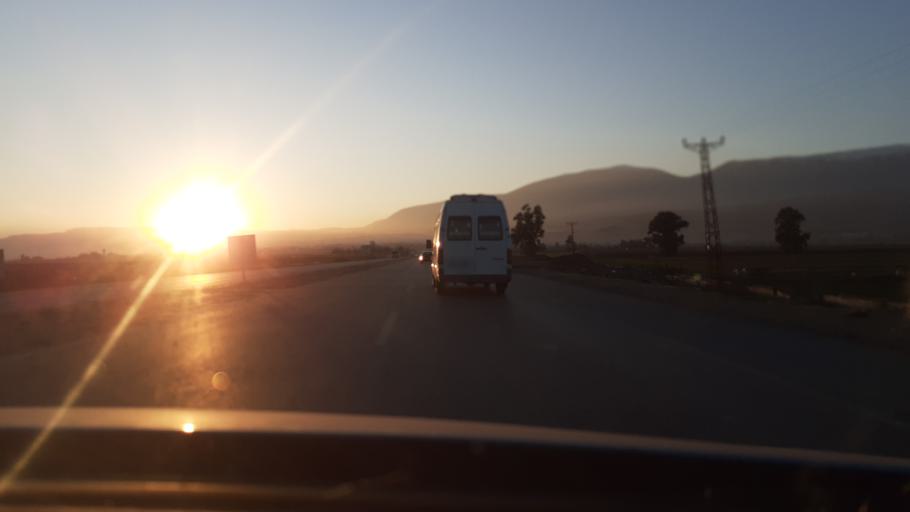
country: TR
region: Hatay
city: Kirikhan
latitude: 36.5047
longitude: 36.4100
